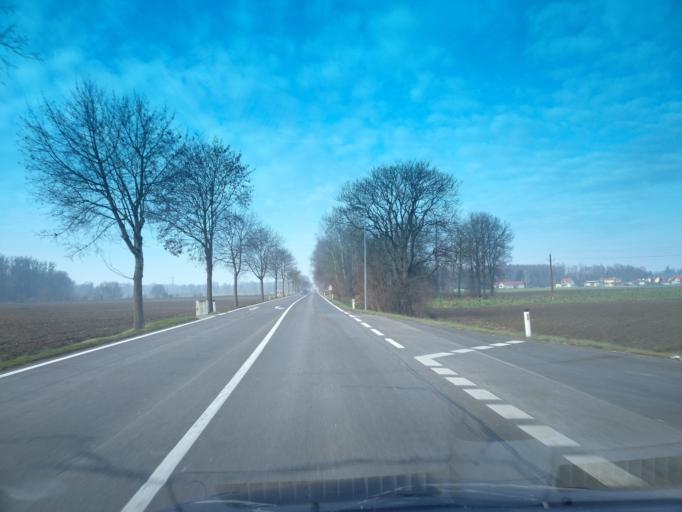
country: AT
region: Styria
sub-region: Politischer Bezirk Leibnitz
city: Strass in Steiermark
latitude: 46.7173
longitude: 15.6283
